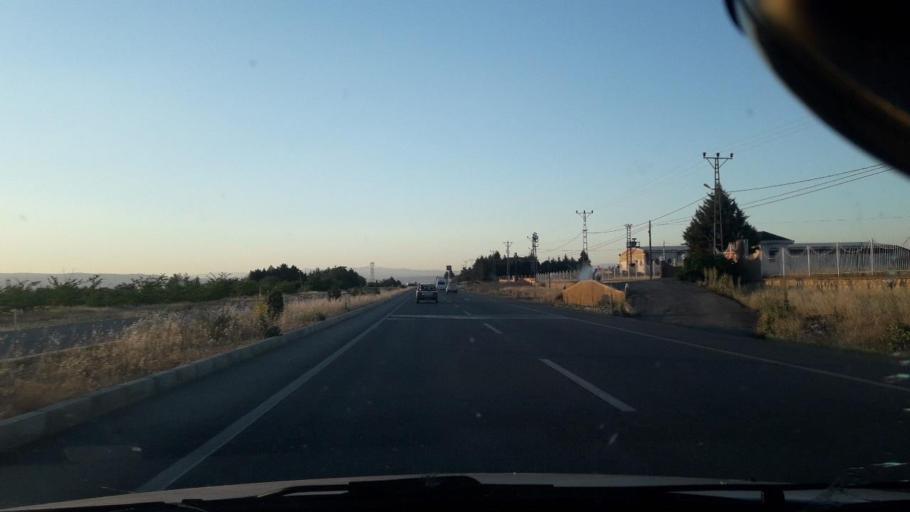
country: TR
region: Malatya
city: Yesilyurt
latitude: 38.3983
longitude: 38.2236
